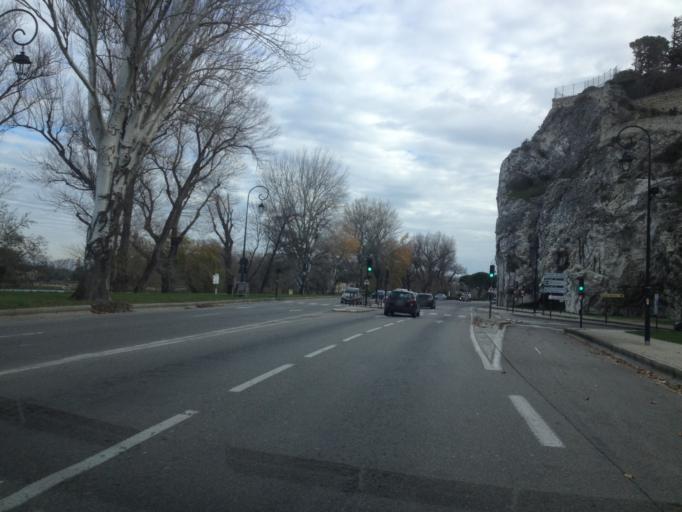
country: FR
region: Provence-Alpes-Cote d'Azur
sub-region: Departement du Vaucluse
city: Avignon
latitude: 43.9534
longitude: 4.8060
